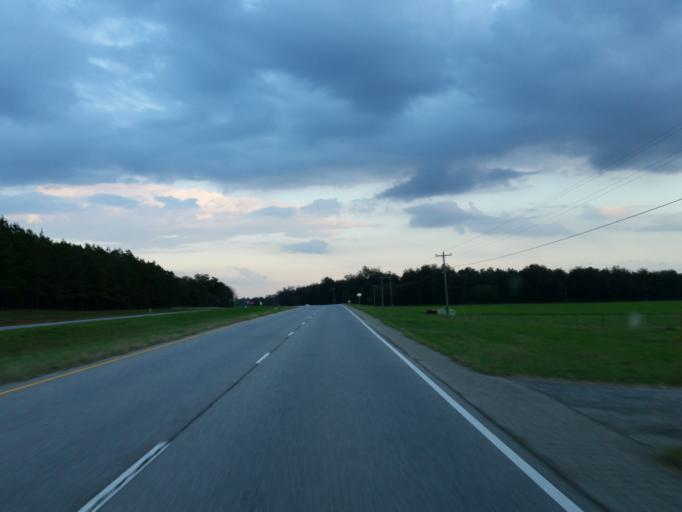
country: US
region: Georgia
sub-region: Pulaski County
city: Hawkinsville
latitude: 32.3156
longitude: -83.5356
